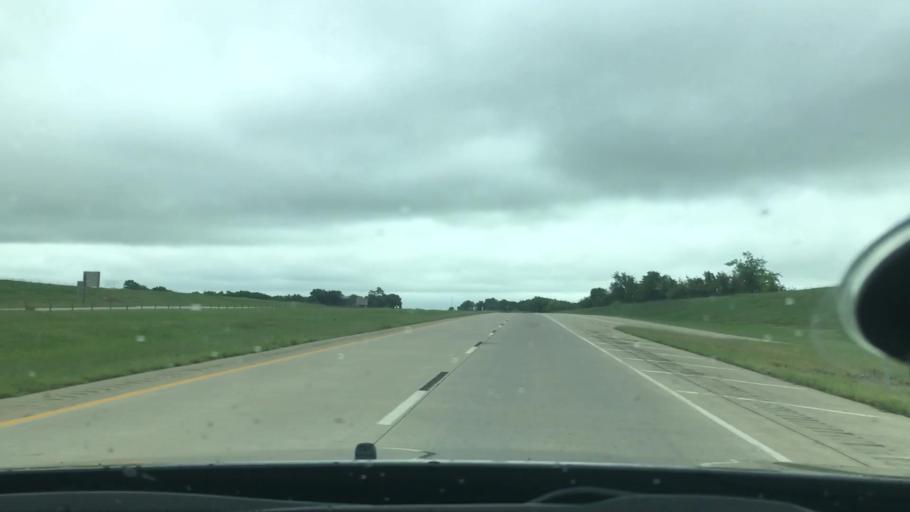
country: US
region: Oklahoma
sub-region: McIntosh County
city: Checotah
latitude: 35.4573
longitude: -95.5909
